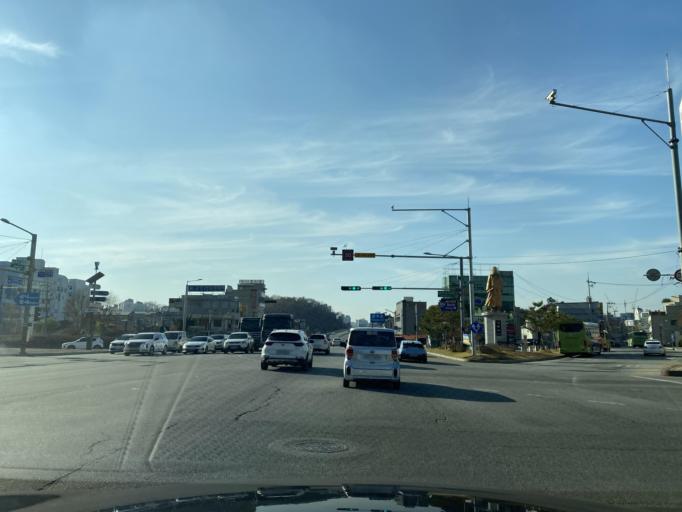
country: KR
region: Chungcheongnam-do
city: Cheonan
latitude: 36.7985
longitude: 127.1539
